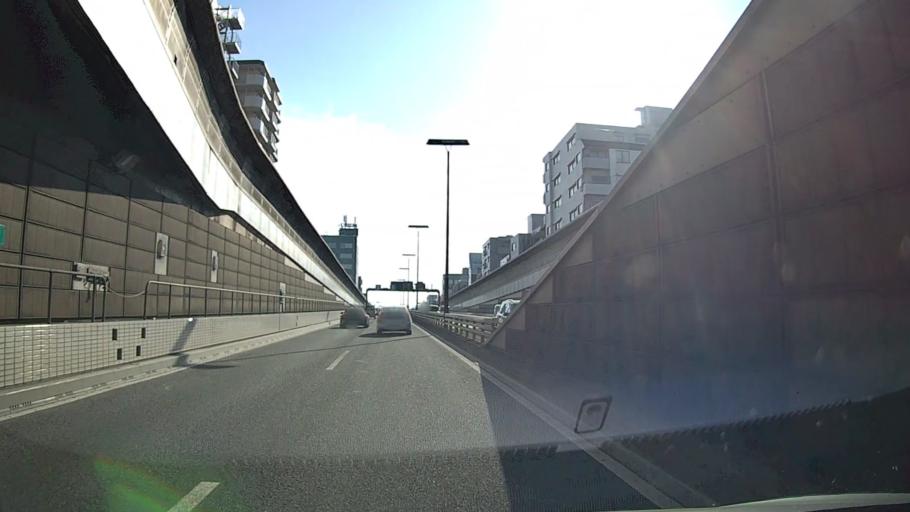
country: JP
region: Tokyo
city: Musashino
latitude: 35.7186
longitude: 139.6161
